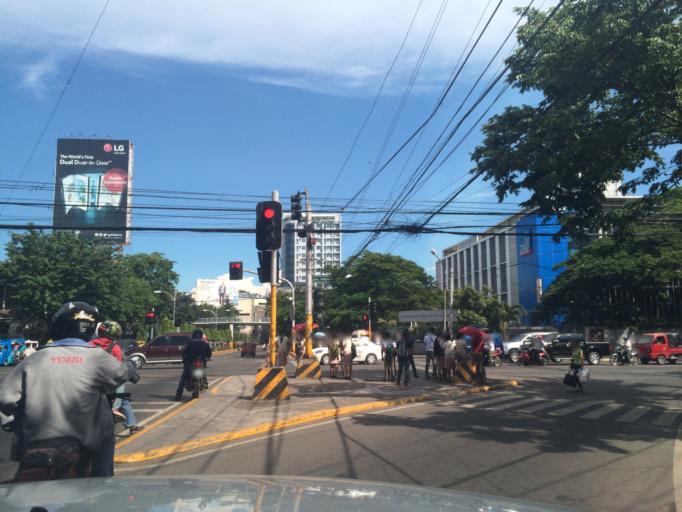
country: PH
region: Central Visayas
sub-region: Cebu City
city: Calero
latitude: 10.2998
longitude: 123.8967
